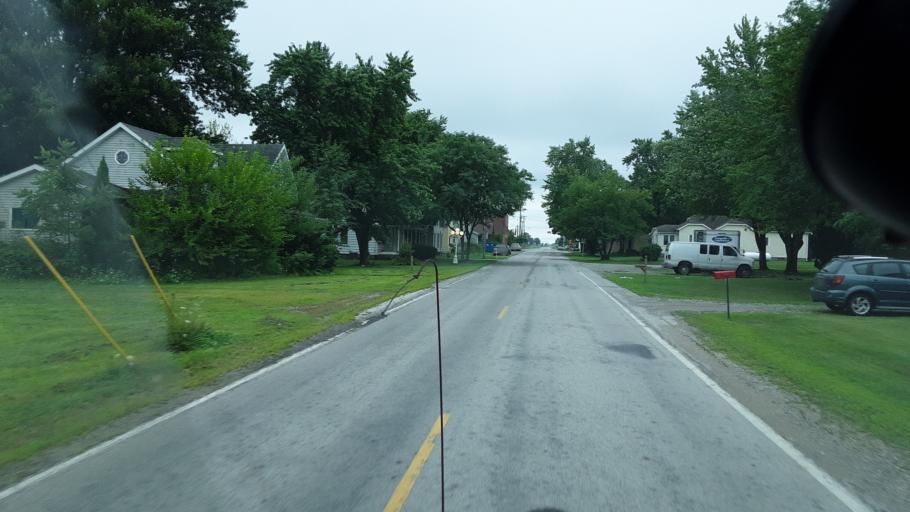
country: US
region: Indiana
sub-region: Wells County
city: Bluffton
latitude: 40.7791
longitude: -85.0907
